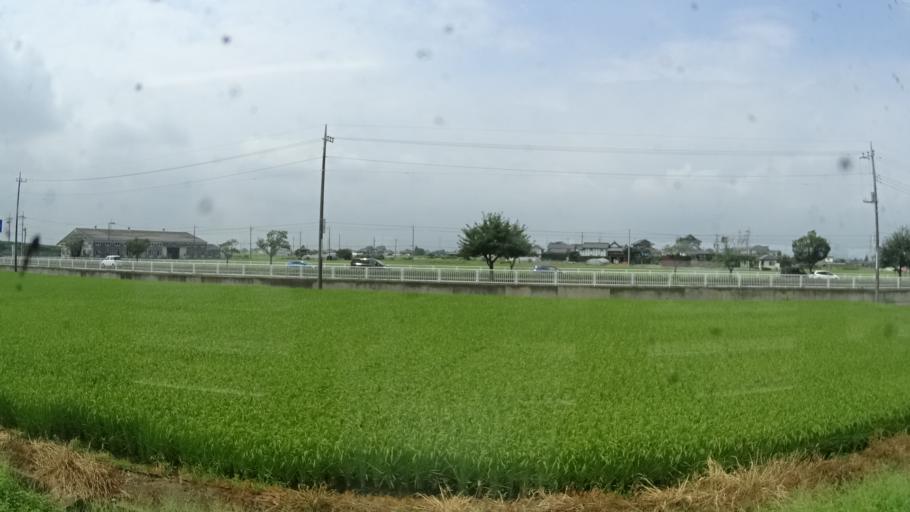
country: JP
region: Ibaraki
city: Shimodate
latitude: 36.3380
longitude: 139.9722
